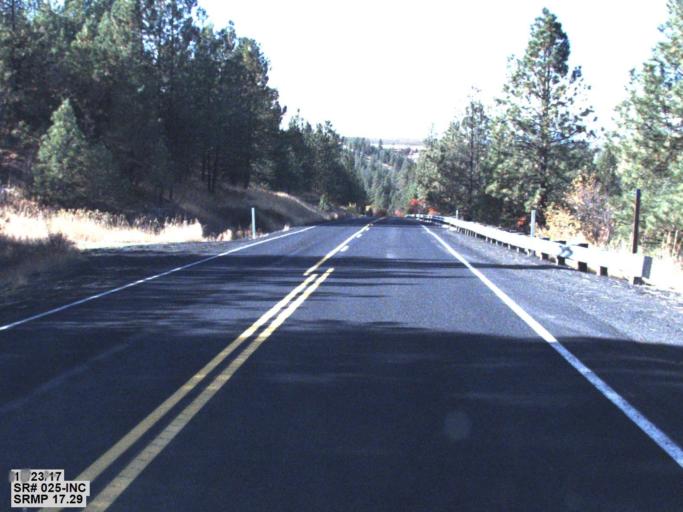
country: US
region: Washington
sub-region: Lincoln County
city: Davenport
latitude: 47.8642
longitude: -118.2501
